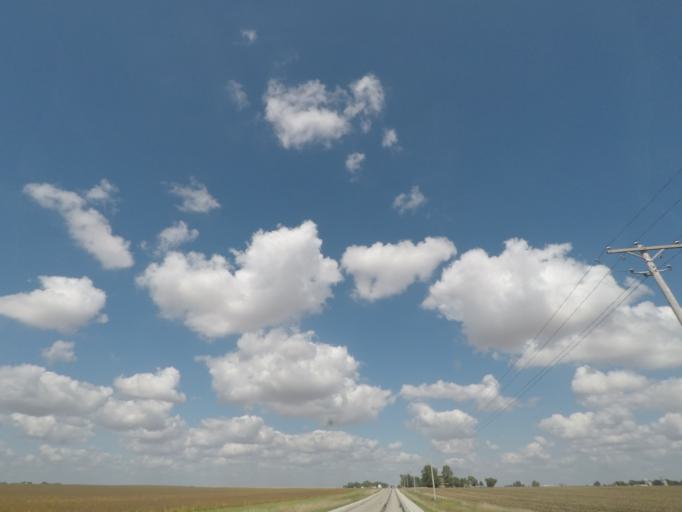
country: US
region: Iowa
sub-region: Story County
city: Nevada
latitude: 42.0587
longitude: -93.4056
